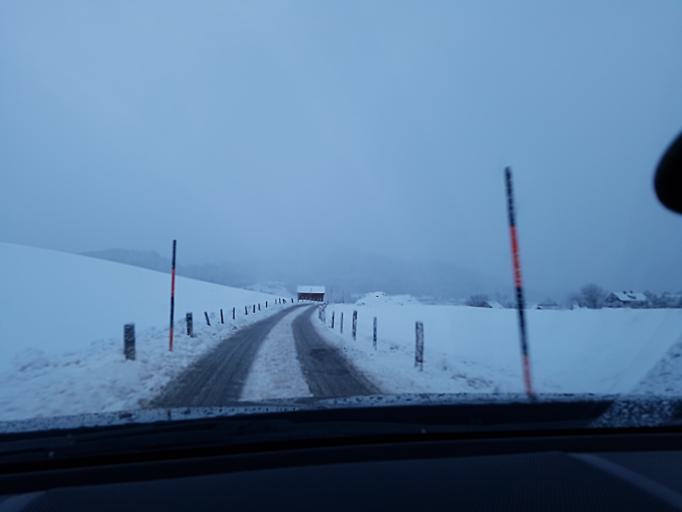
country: AT
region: Styria
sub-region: Politischer Bezirk Liezen
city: Altaussee
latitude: 47.6291
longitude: 13.7700
